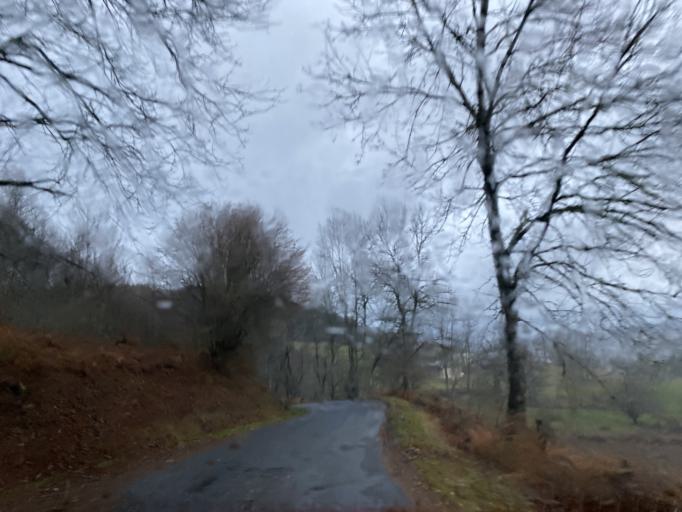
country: FR
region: Auvergne
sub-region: Departement du Puy-de-Dome
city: La Monnerie-le-Montel
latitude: 45.8469
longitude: 3.6067
